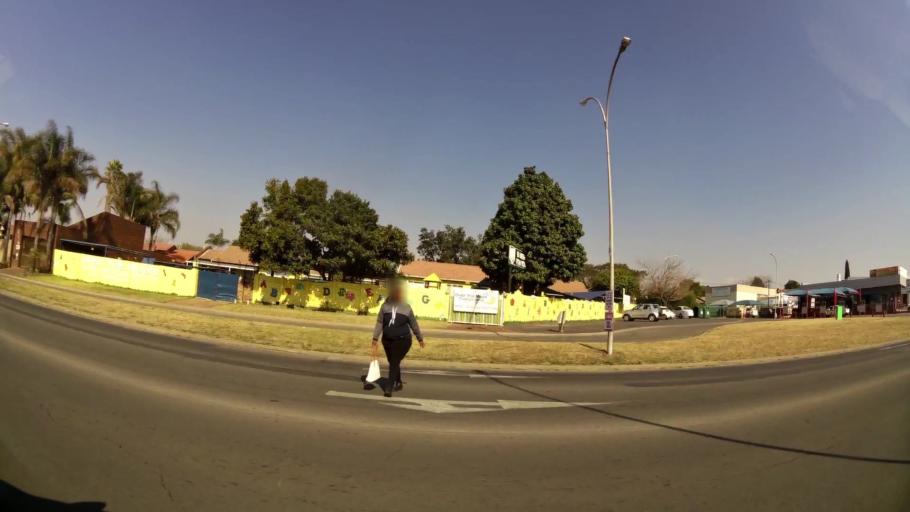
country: ZA
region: Gauteng
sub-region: City of Johannesburg Metropolitan Municipality
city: Modderfontein
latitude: -26.1248
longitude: 28.1712
